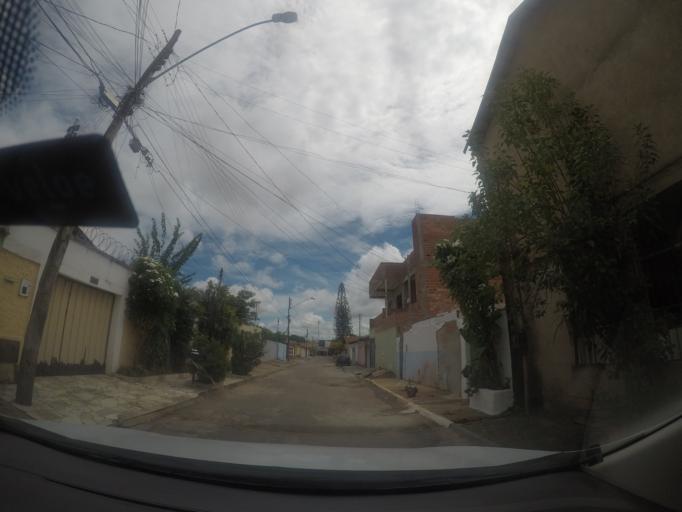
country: BR
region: Goias
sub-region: Goiania
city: Goiania
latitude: -16.6626
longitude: -49.3004
